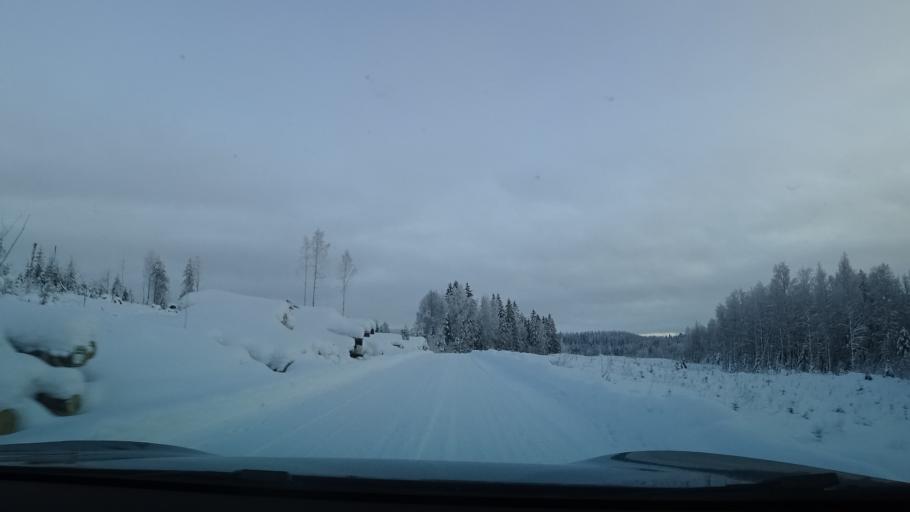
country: FI
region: North Karelia
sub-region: Pielisen Karjala
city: Lieksa
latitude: 63.1051
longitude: 29.7539
